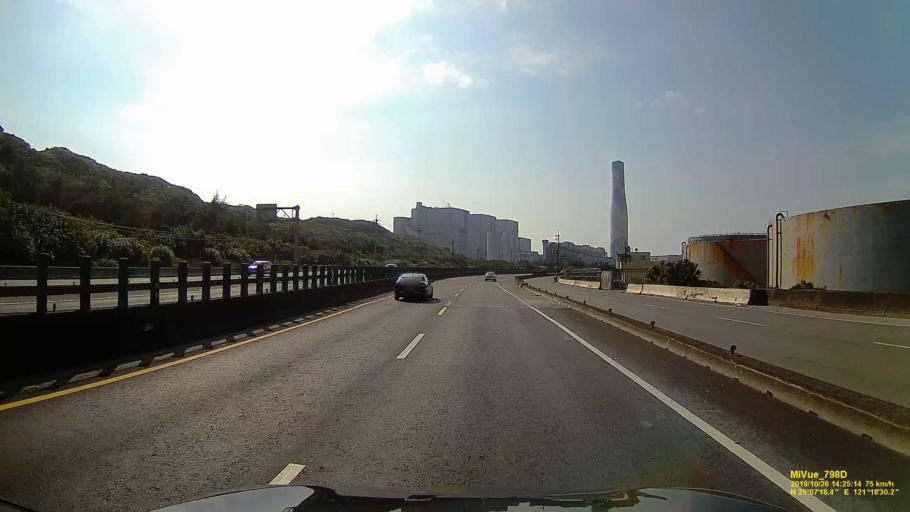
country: TW
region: Taiwan
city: Taoyuan City
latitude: 25.1218
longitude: 121.3079
